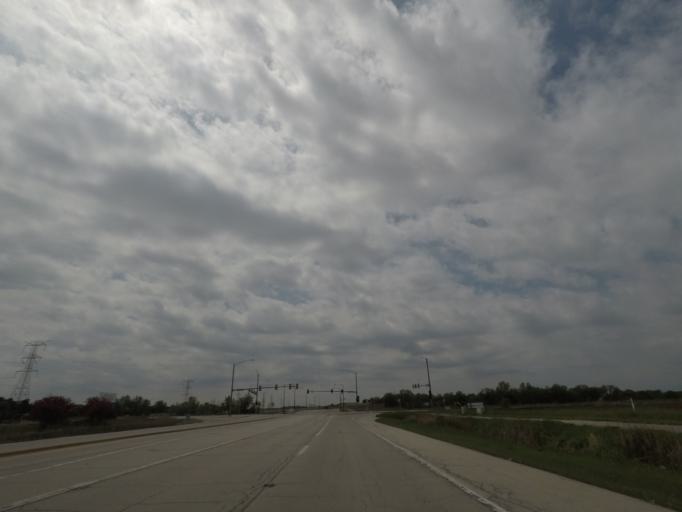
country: US
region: Illinois
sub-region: Winnebago County
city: Cherry Valley
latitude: 42.3204
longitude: -88.9479
